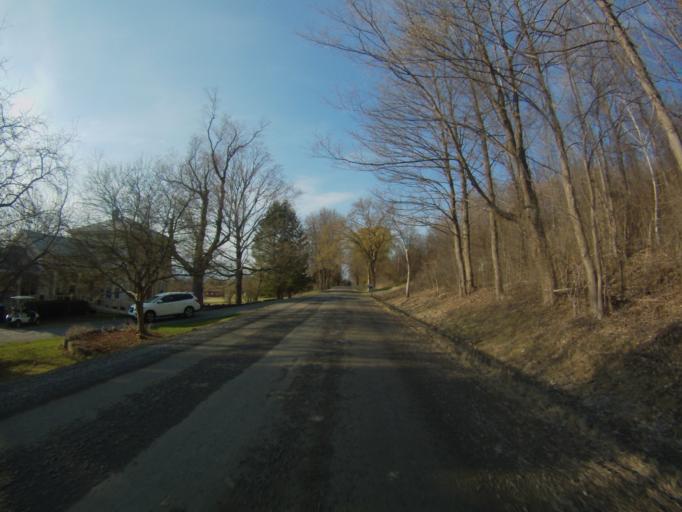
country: US
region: Vermont
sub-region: Addison County
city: Vergennes
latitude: 44.0573
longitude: -73.2925
